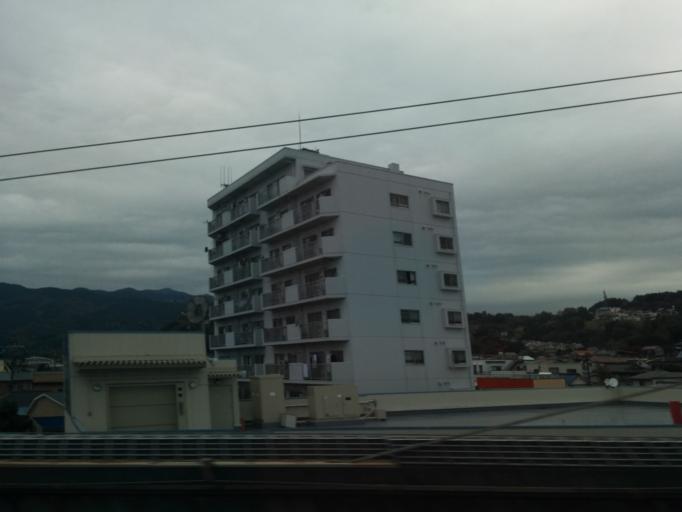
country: JP
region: Kanagawa
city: Odawara
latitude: 35.2456
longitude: 139.1467
